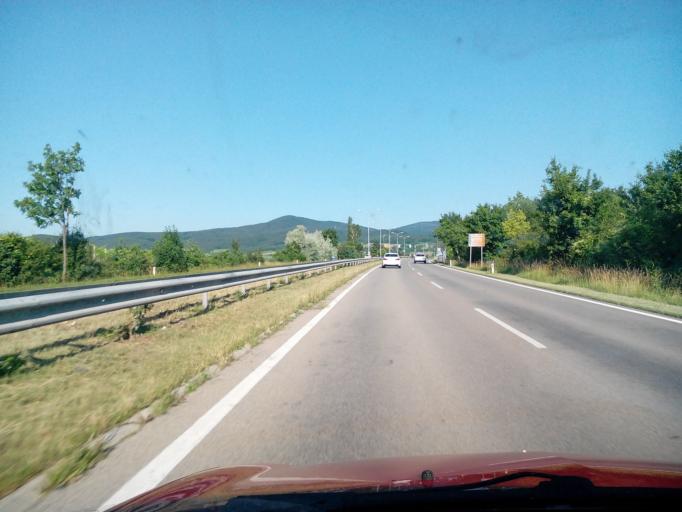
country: AT
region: Lower Austria
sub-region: Politischer Bezirk Baden
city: Baden
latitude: 47.9941
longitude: 16.2381
